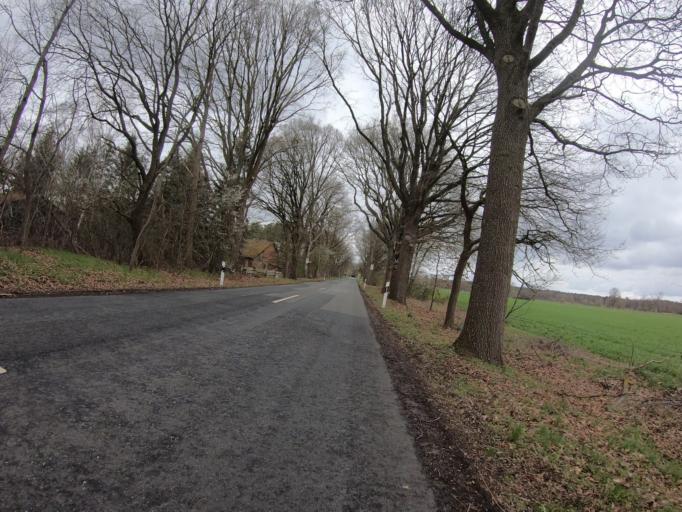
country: DE
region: Lower Saxony
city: Leiferde
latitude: 52.4946
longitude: 10.4366
